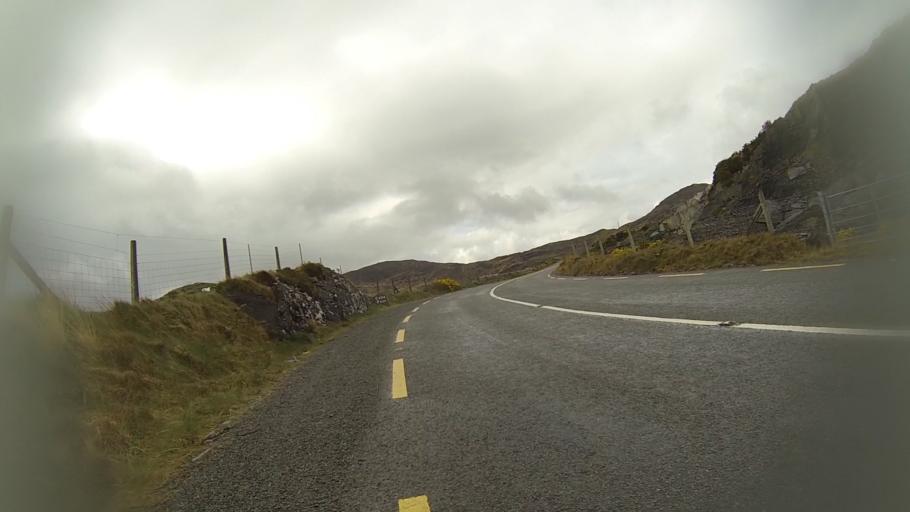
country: IE
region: Munster
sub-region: Ciarrai
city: Kenmare
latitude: 51.7997
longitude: -9.5773
